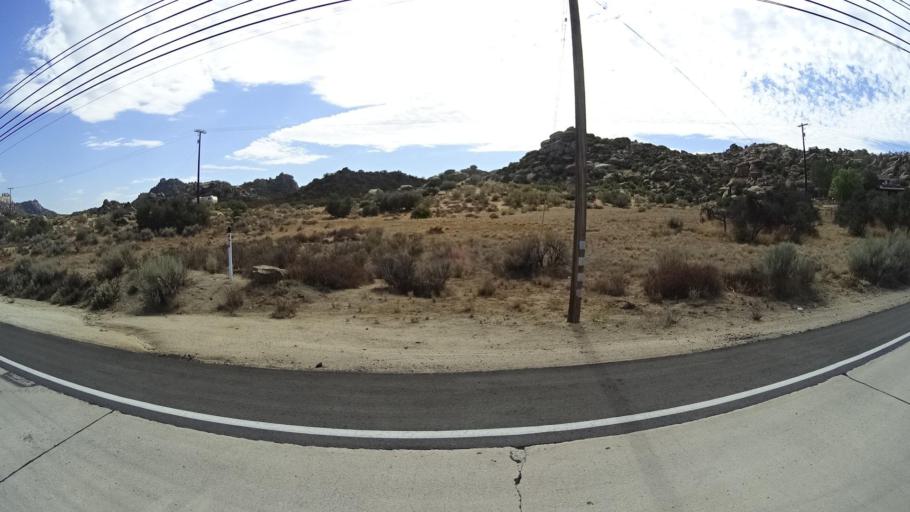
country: MX
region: Baja California
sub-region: Tecate
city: Cereso del Hongo
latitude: 32.6623
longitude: -116.2581
